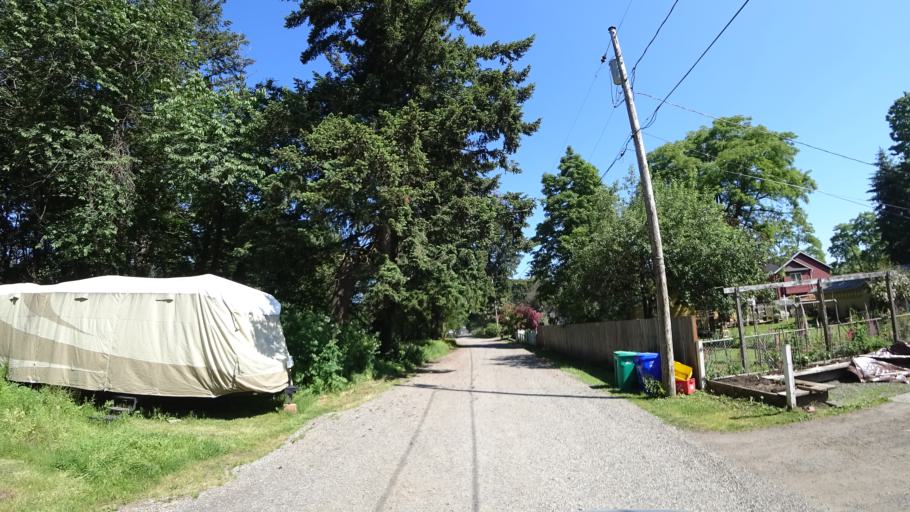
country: US
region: Oregon
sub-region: Multnomah County
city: Lents
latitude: 45.4807
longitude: -122.5410
